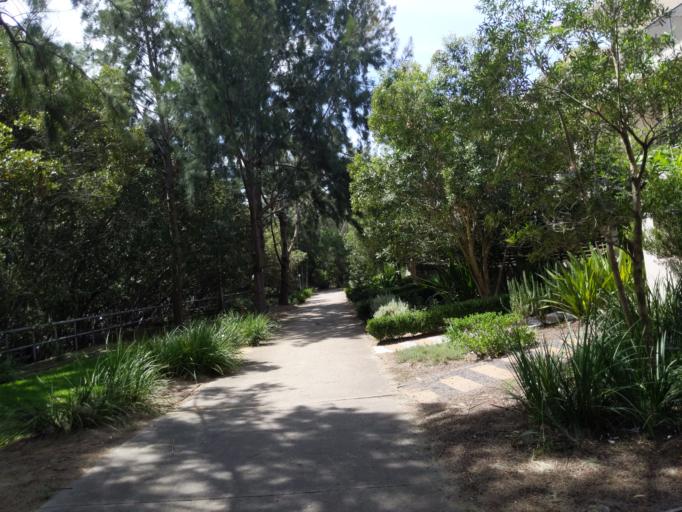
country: AU
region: New South Wales
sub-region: Canada Bay
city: Concord
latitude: -33.8426
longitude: 151.1040
